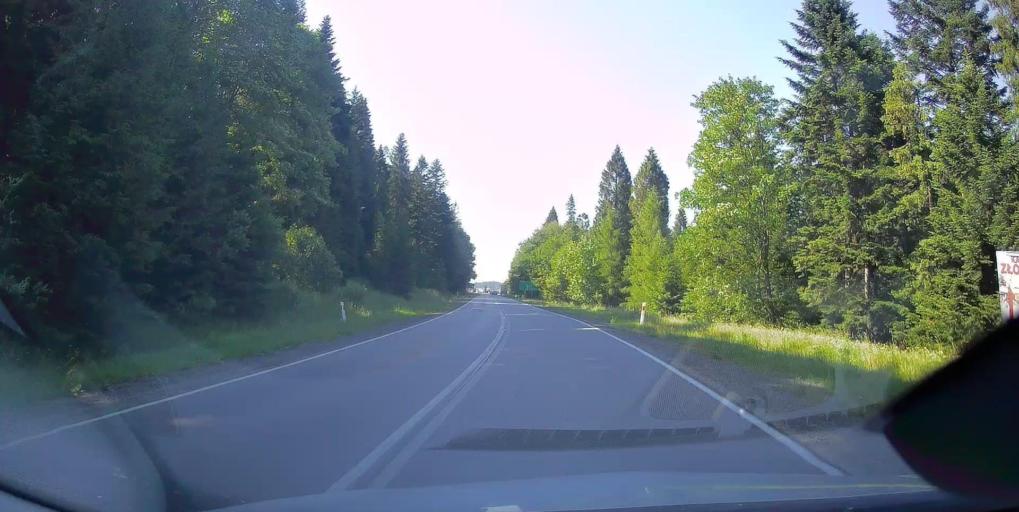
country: PL
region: Lesser Poland Voivodeship
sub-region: Powiat nowosadecki
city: Krynica-Zdroj
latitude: 49.4603
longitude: 20.9575
